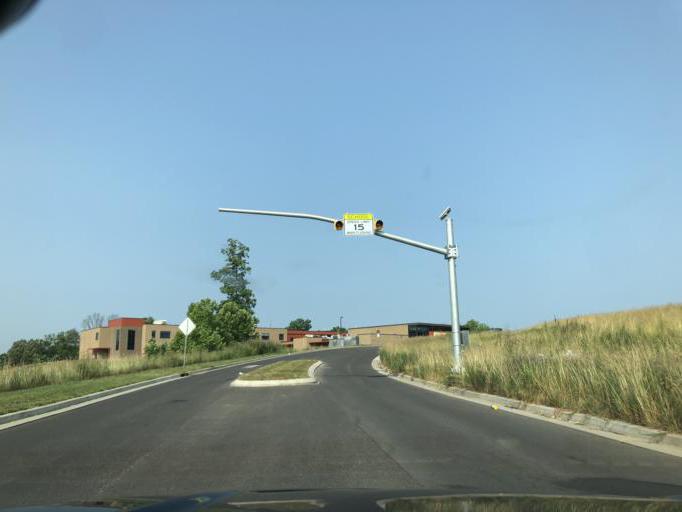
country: US
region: Tennessee
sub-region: Rutherford County
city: La Vergne
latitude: 36.0500
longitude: -86.6384
